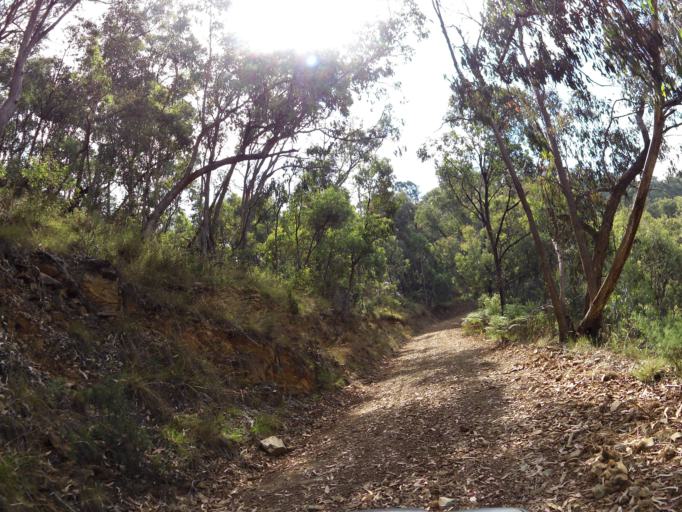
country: AU
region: Victoria
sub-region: Alpine
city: Mount Beauty
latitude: -36.7783
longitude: 147.0113
